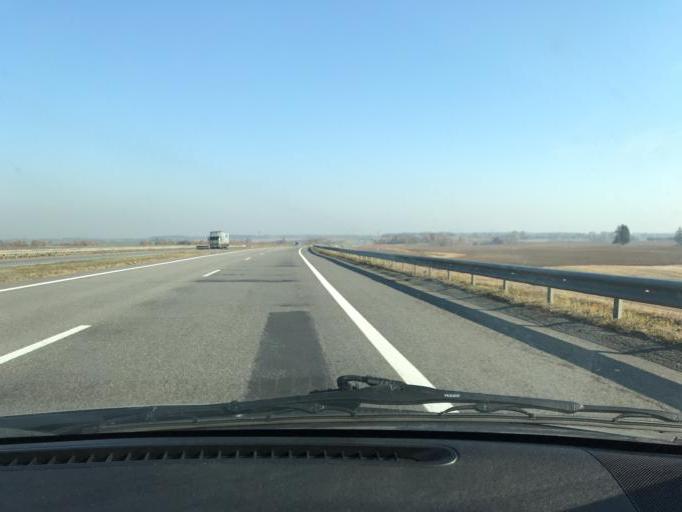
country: BY
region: Vitebsk
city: Baran'
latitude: 54.5615
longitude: 30.2883
